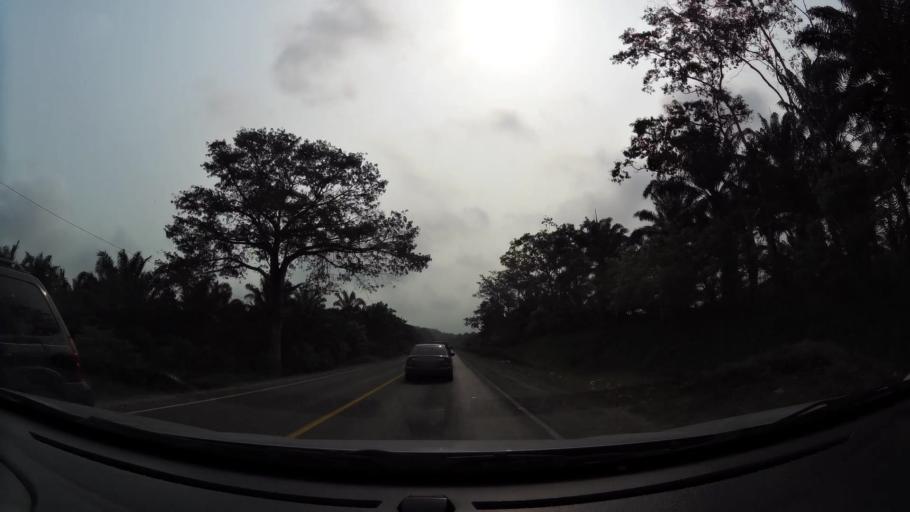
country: HN
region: Yoro
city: Toyos
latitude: 15.5527
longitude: -87.6488
